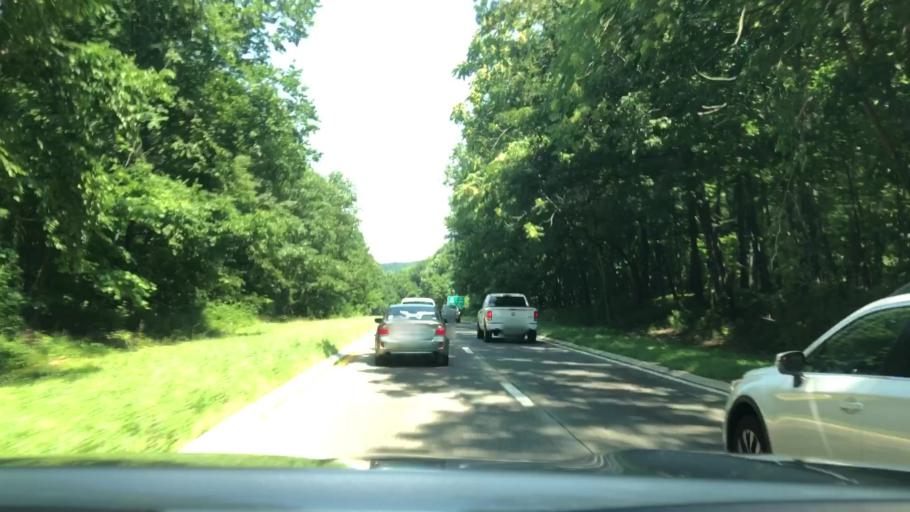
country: US
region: New York
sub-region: Rockland County
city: New Hempstead
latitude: 41.1605
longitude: -74.0274
